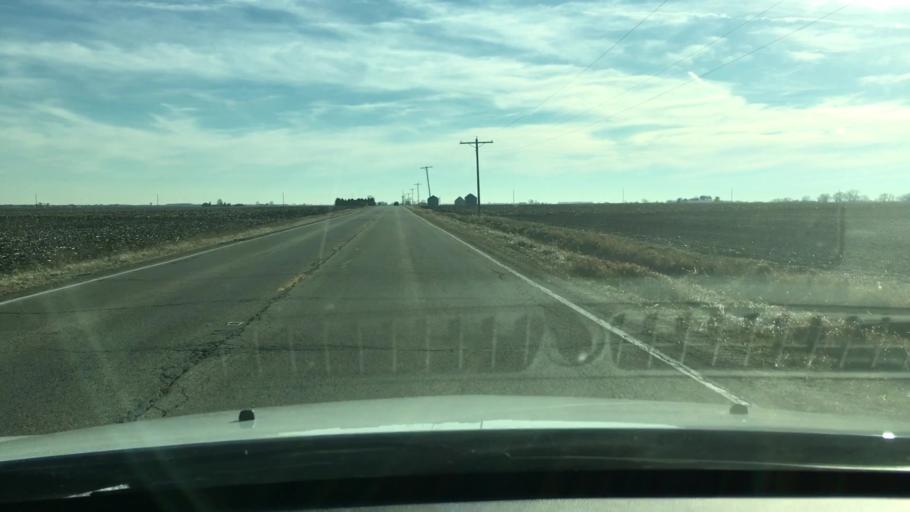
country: US
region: Illinois
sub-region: LaSalle County
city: Mendota
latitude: 41.4482
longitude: -89.1268
